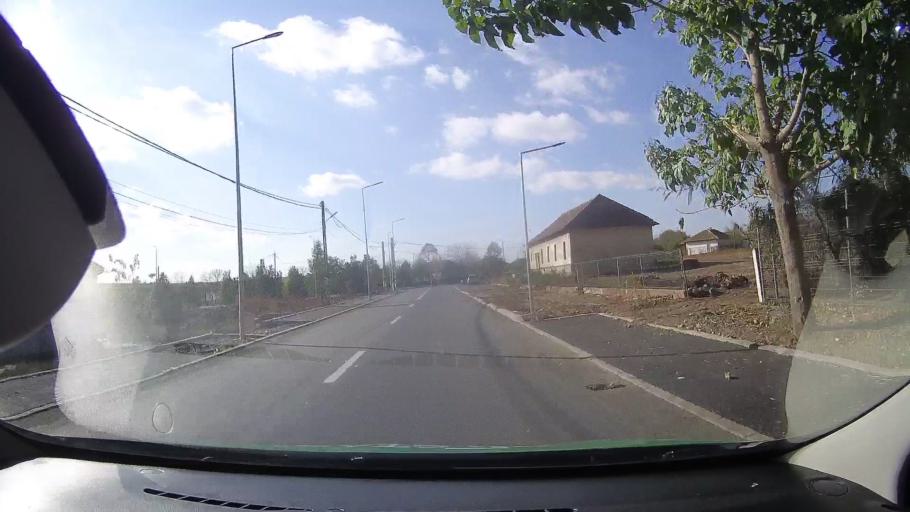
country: RO
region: Constanta
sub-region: Comuna Cogealac
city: Cogealac
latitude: 44.5558
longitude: 28.5616
